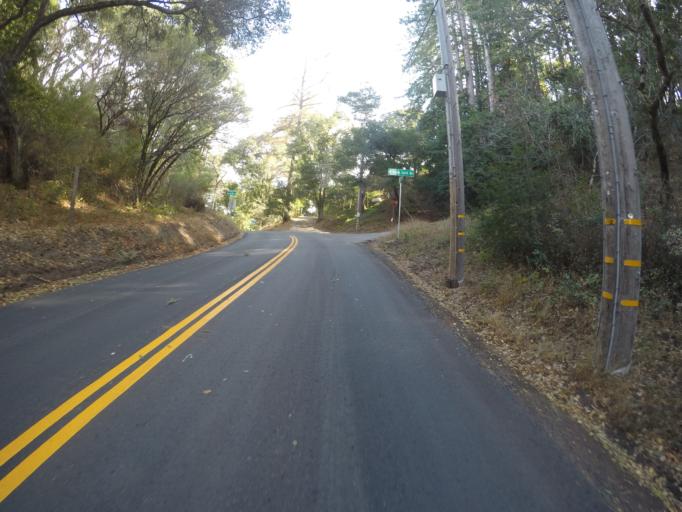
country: US
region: California
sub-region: Santa Cruz County
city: Scotts Valley
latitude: 37.0557
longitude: -121.9632
